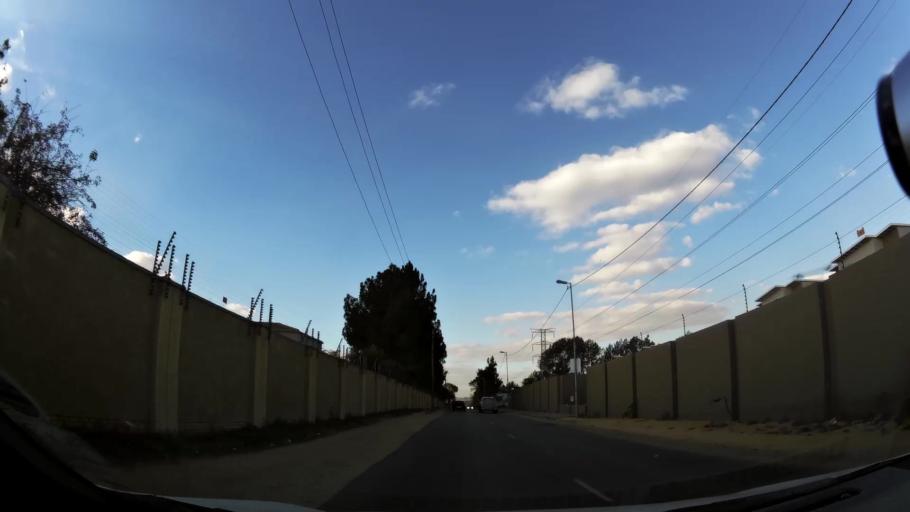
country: ZA
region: Gauteng
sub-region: City of Johannesburg Metropolitan Municipality
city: Diepsloot
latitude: -26.0020
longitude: 27.9884
